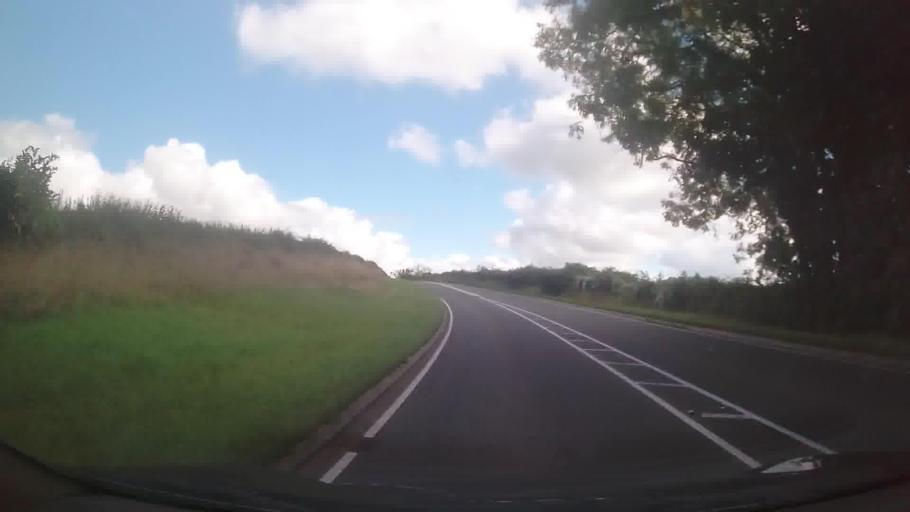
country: GB
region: Wales
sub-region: Pembrokeshire
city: Pembroke
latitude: 51.6815
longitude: -4.8880
